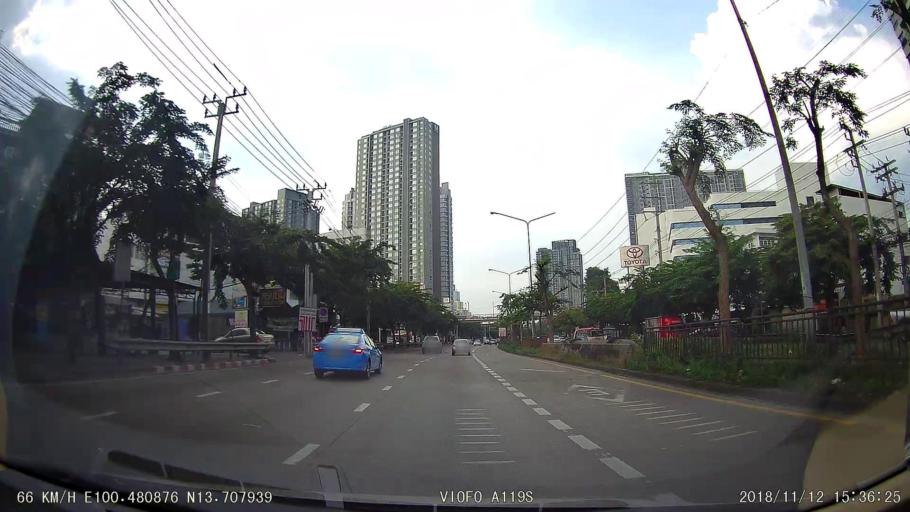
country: TH
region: Bangkok
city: Bangkok Yai
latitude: 13.7080
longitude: 100.4808
